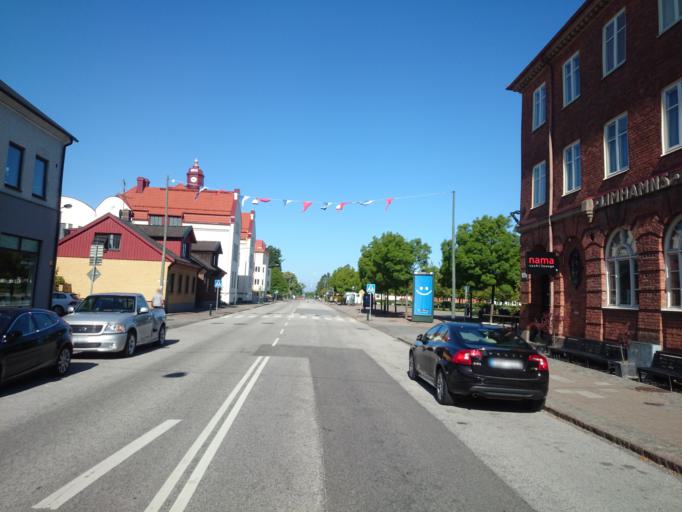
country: SE
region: Skane
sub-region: Malmo
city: Bunkeflostrand
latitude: 55.5823
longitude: 12.9287
